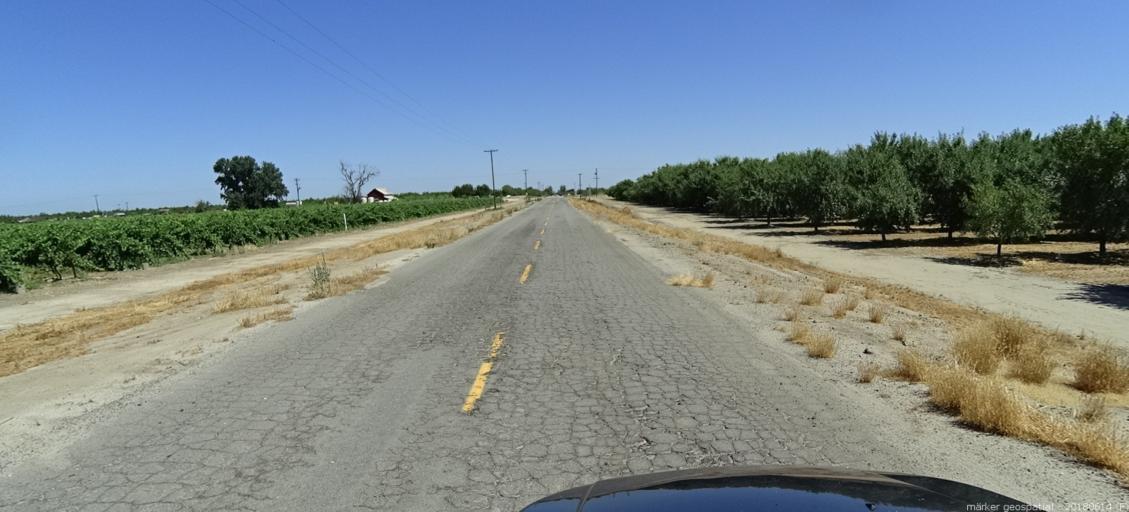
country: US
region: California
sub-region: Madera County
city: Fairmead
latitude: 36.9800
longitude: -120.1842
